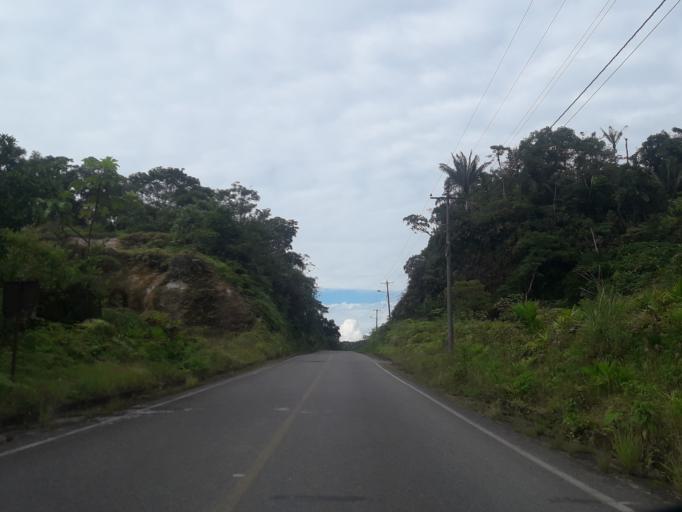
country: EC
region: Napo
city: Tena
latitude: -1.0417
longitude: -77.8983
